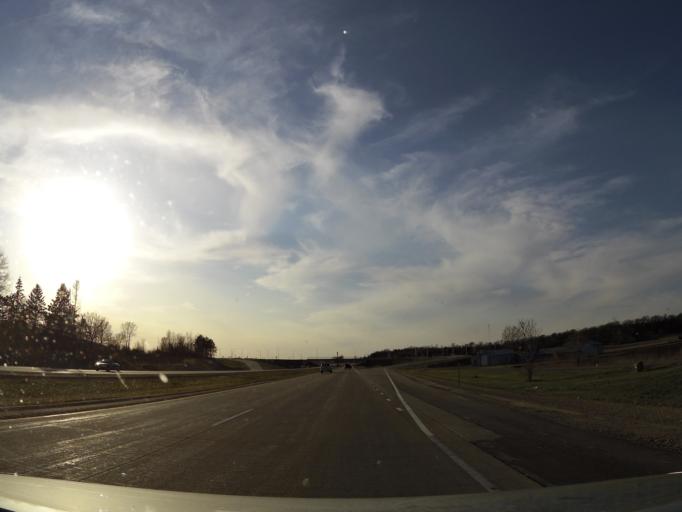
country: US
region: Wisconsin
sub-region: Pierce County
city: River Falls
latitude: 44.8958
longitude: -92.6428
